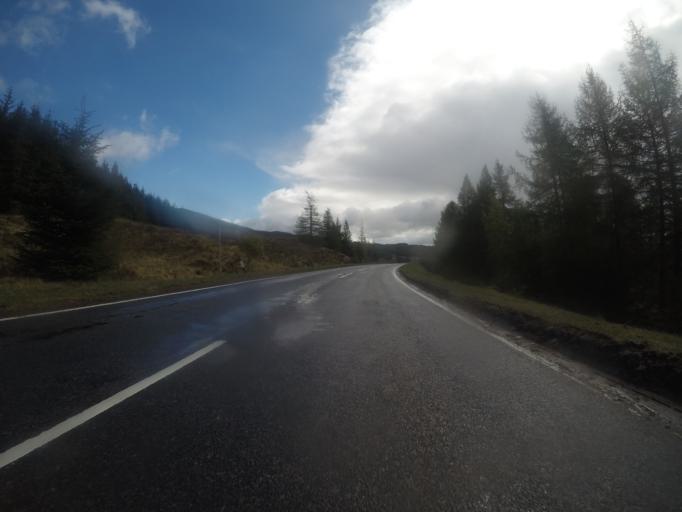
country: GB
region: Scotland
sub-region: Highland
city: Spean Bridge
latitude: 57.0876
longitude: -4.9743
